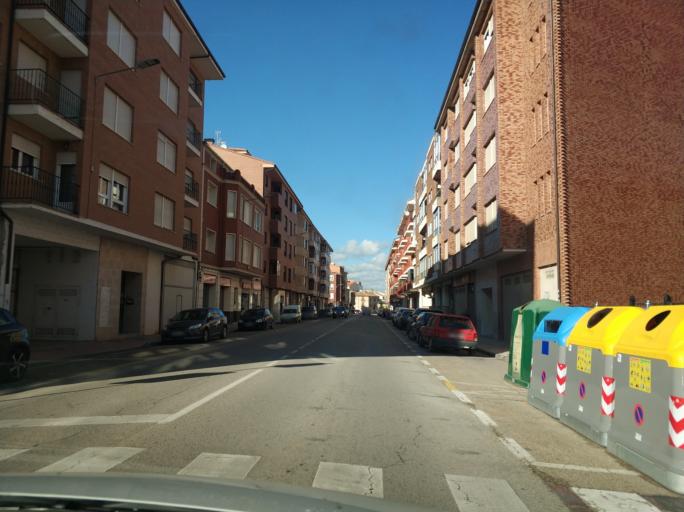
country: ES
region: Castille and Leon
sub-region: Provincia de Soria
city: Almazan
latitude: 41.4835
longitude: -2.5300
